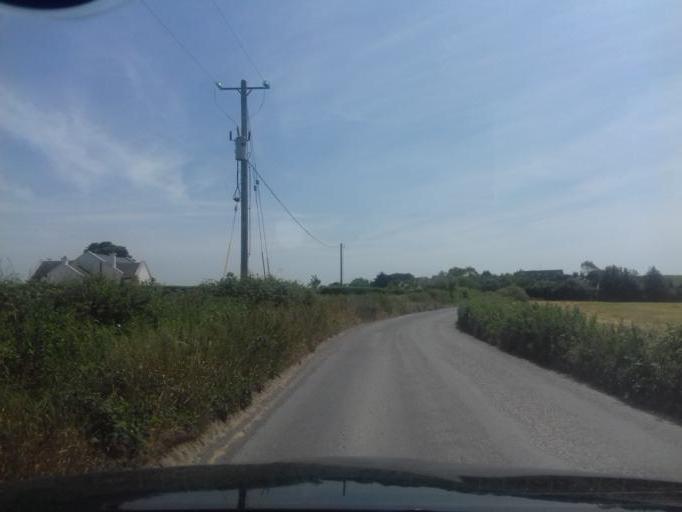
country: IE
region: Leinster
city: Lusk
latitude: 53.5347
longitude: -6.1792
